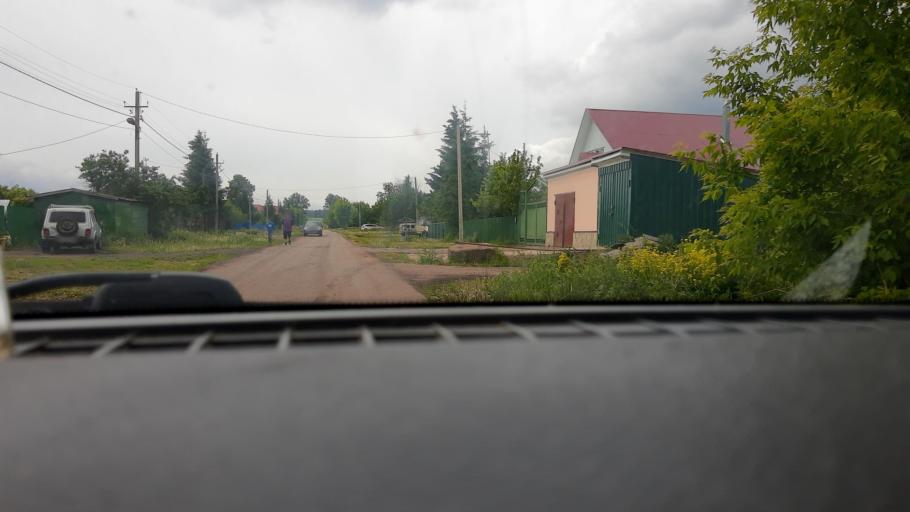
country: RU
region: Bashkortostan
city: Dmitriyevka
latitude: 54.7216
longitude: 55.4938
